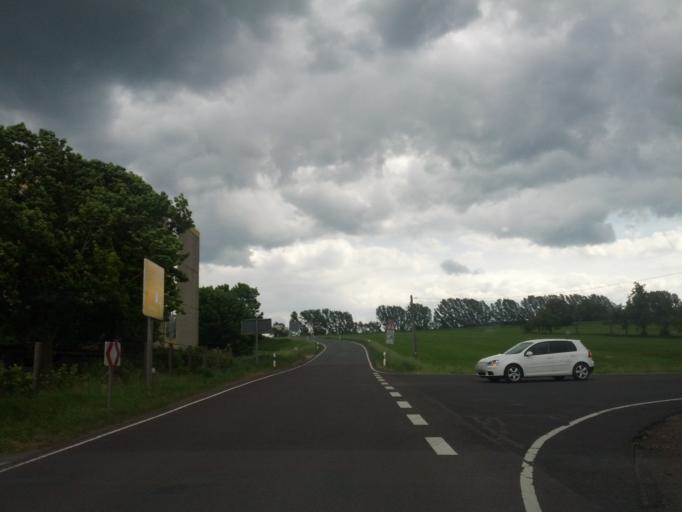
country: DE
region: Thuringia
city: Friedrichswerth
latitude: 50.9897
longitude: 10.5430
